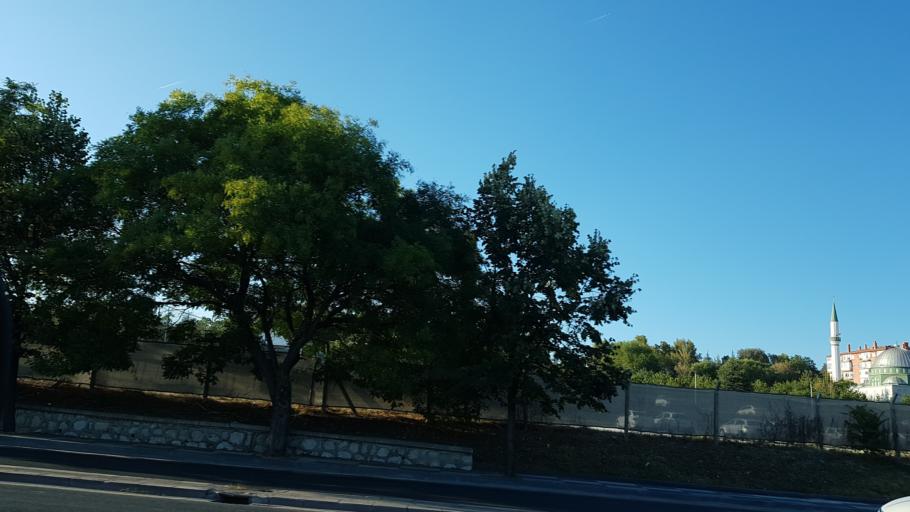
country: TR
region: Ankara
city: Batikent
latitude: 39.9475
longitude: 32.7847
